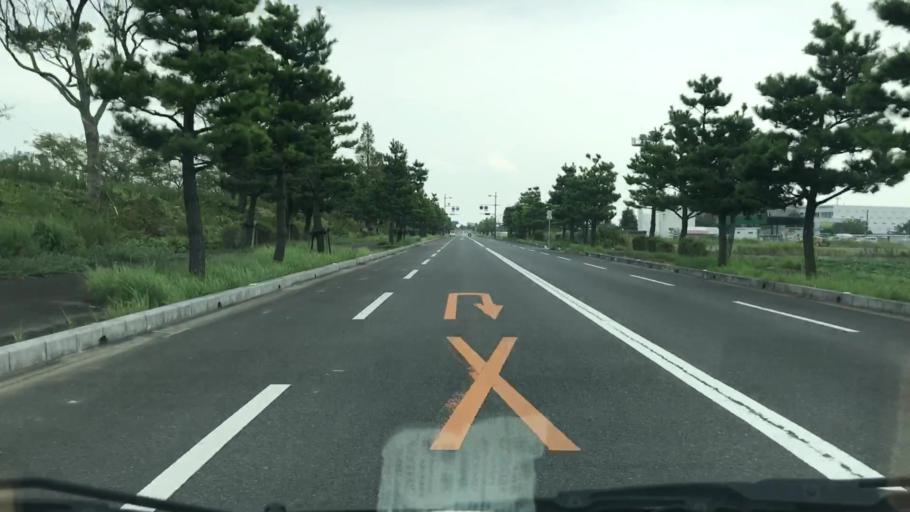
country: JP
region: Saga Prefecture
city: Okawa
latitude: 33.1560
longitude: 130.2999
